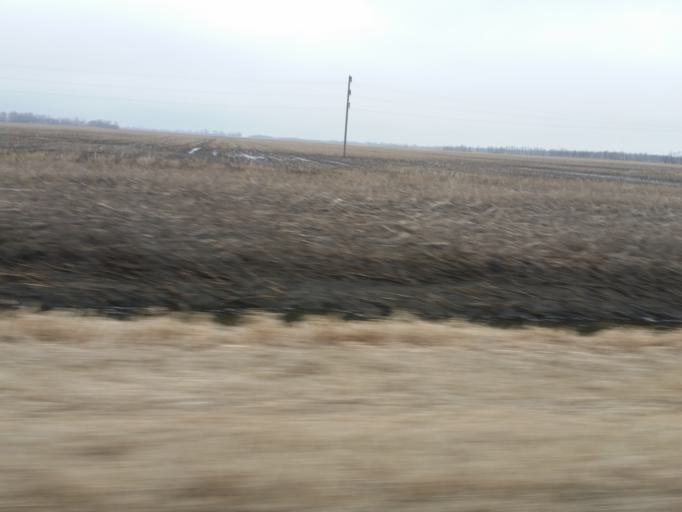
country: US
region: North Dakota
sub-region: Walsh County
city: Grafton
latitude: 48.3532
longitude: -97.1703
